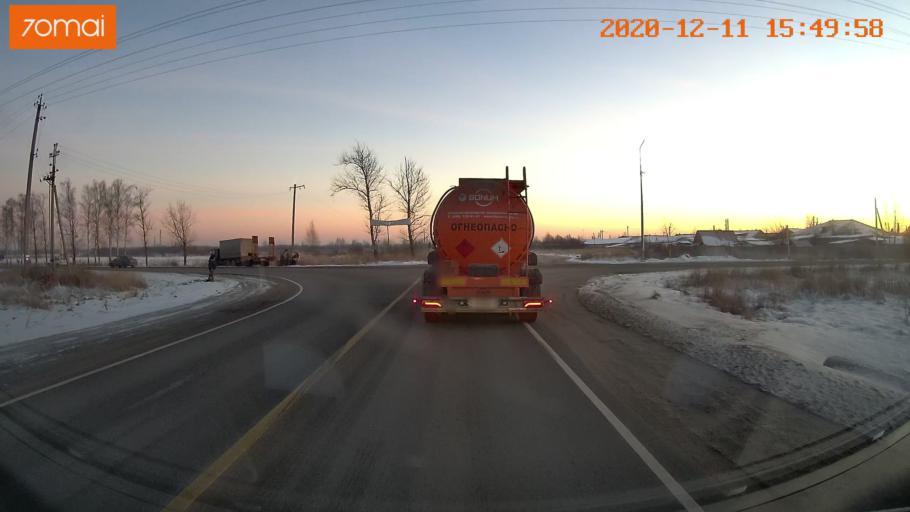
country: RU
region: Ivanovo
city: Novo-Talitsy
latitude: 56.9847
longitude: 40.8784
